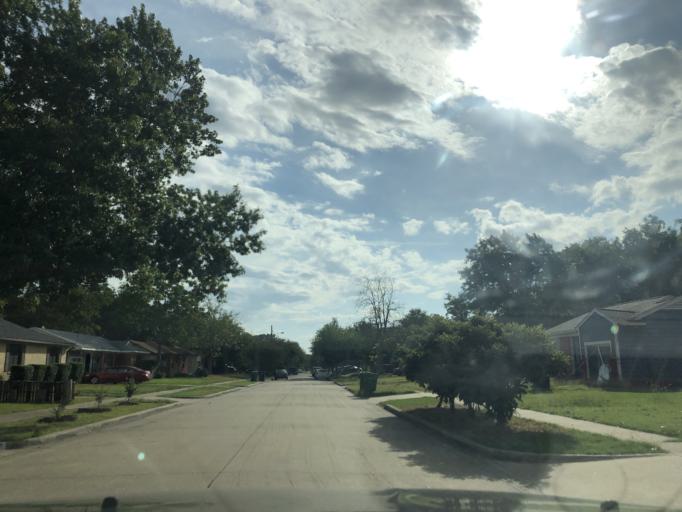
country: US
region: Texas
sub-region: Dallas County
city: Garland
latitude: 32.8825
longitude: -96.6649
